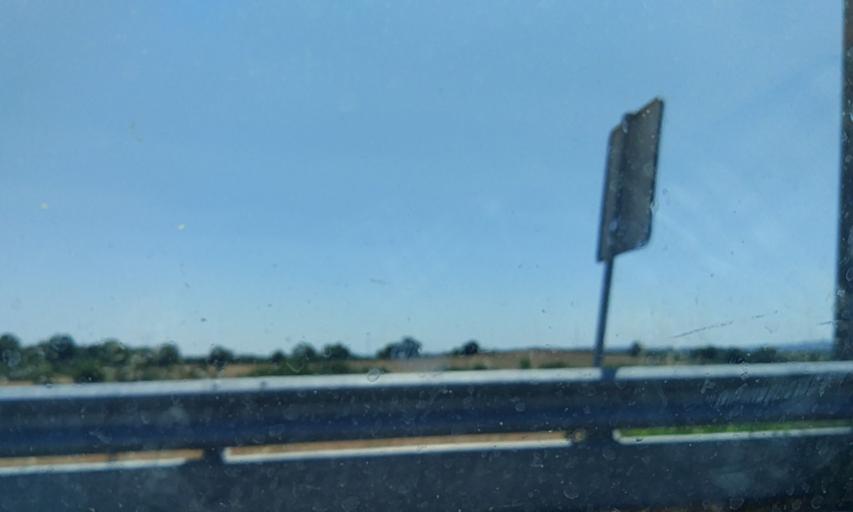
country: PT
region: Braganca
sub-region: Braganca Municipality
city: Braganca
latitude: 41.7622
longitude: -6.7925
